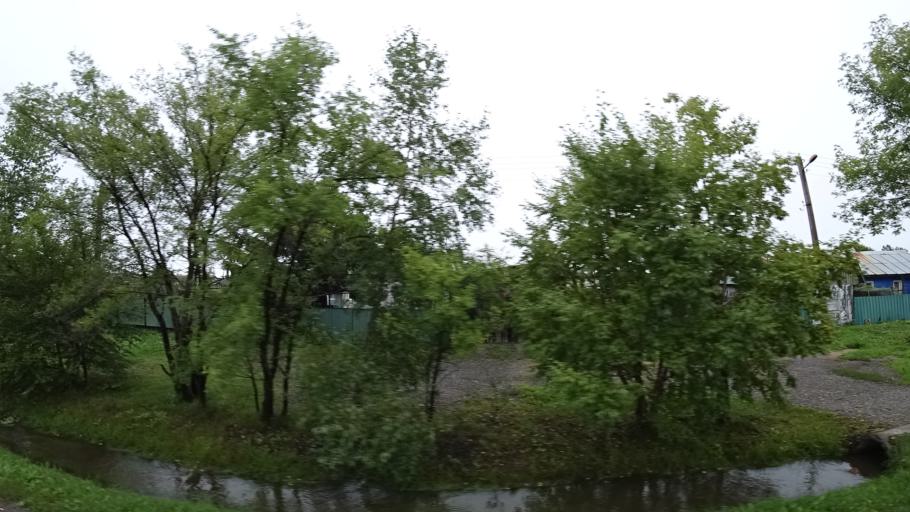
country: RU
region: Primorskiy
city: Monastyrishche
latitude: 44.1992
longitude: 132.4608
